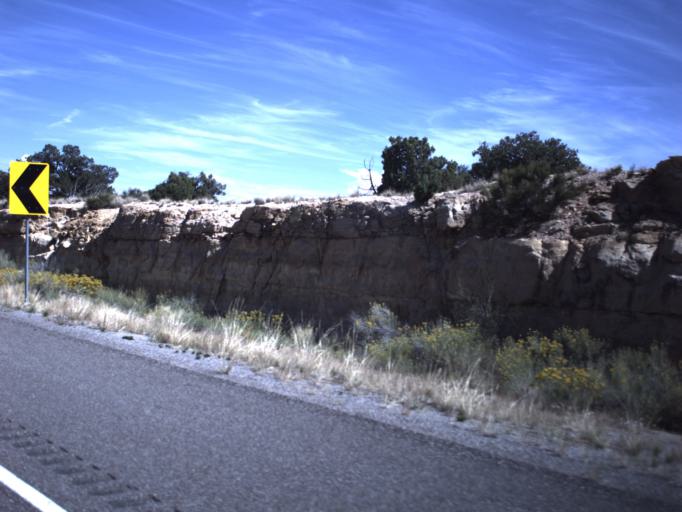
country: US
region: Utah
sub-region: Emery County
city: Castle Dale
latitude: 38.9133
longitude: -110.5058
